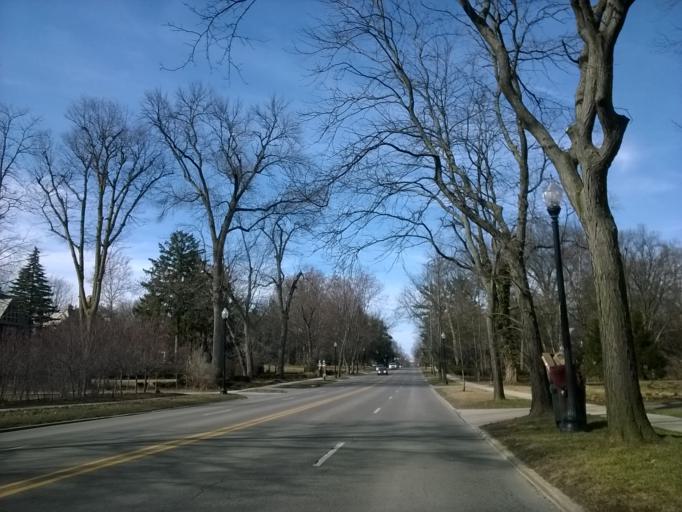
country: US
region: Indiana
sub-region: Marion County
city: Broad Ripple
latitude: 39.8433
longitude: -86.1570
